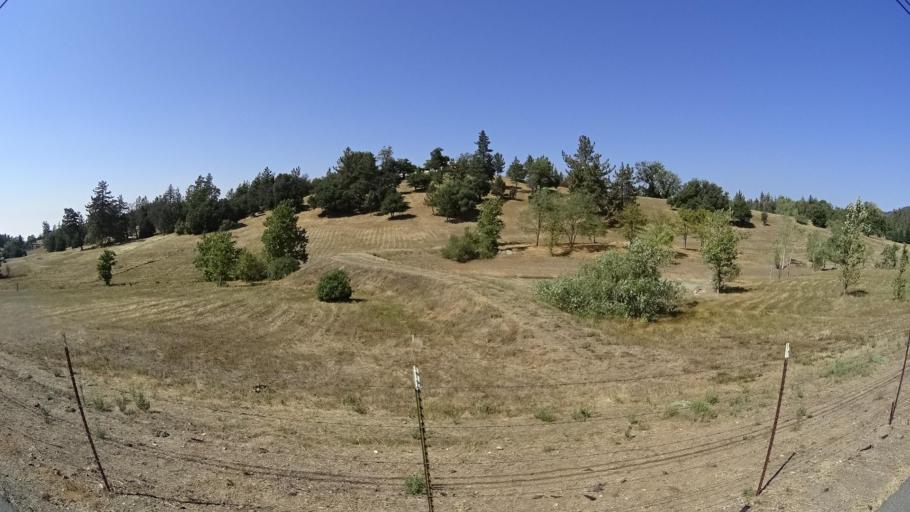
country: US
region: California
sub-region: San Diego County
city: Julian
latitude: 33.0876
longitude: -116.6083
